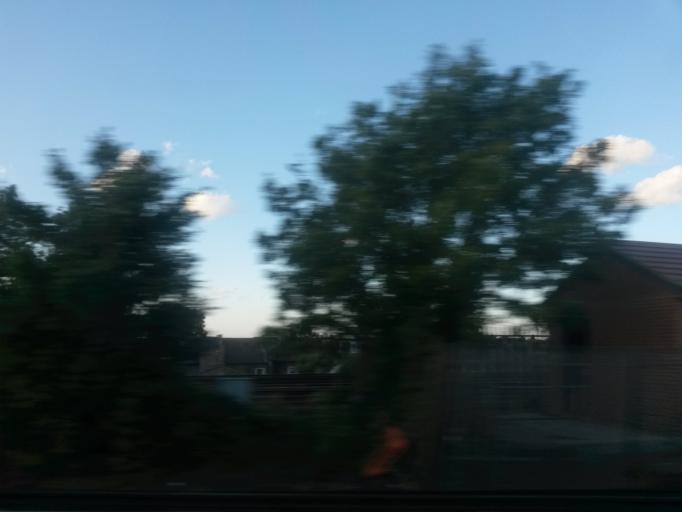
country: GB
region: England
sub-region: Greater London
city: Brixton Hill
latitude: 51.4414
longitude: -0.1450
